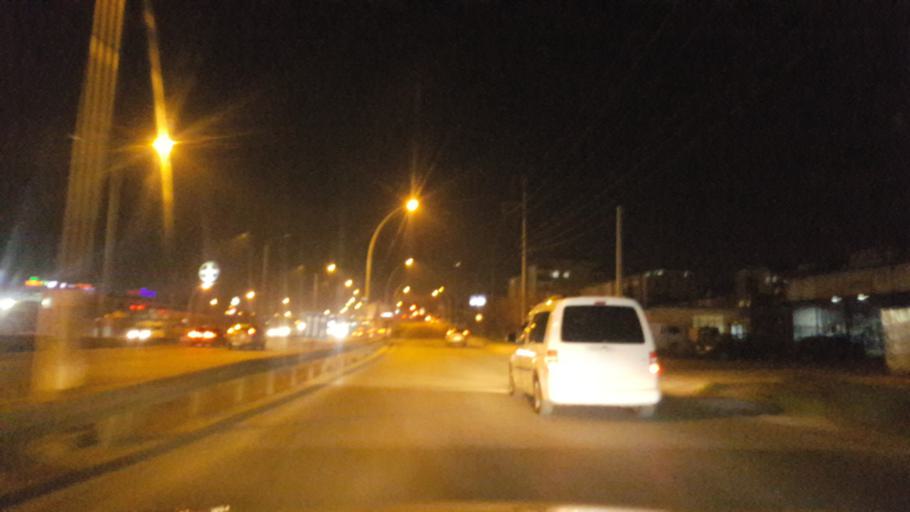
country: TR
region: Kocaeli
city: Gebze
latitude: 40.7990
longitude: 29.4480
